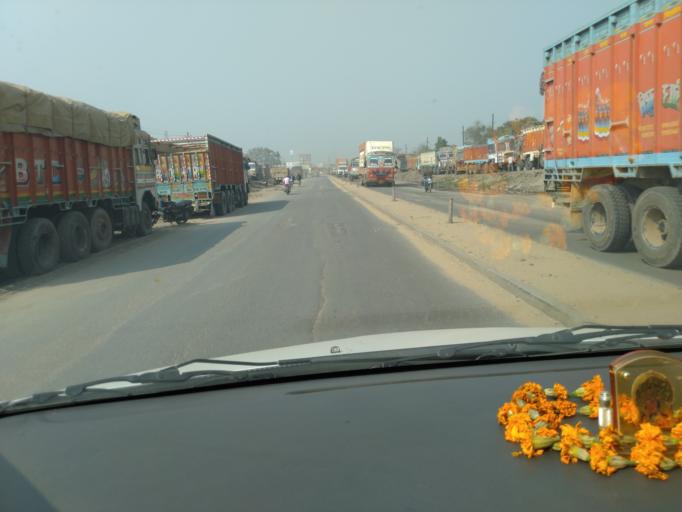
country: IN
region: Bihar
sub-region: Rohtas
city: Dehri
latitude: 24.9108
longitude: 84.1693
